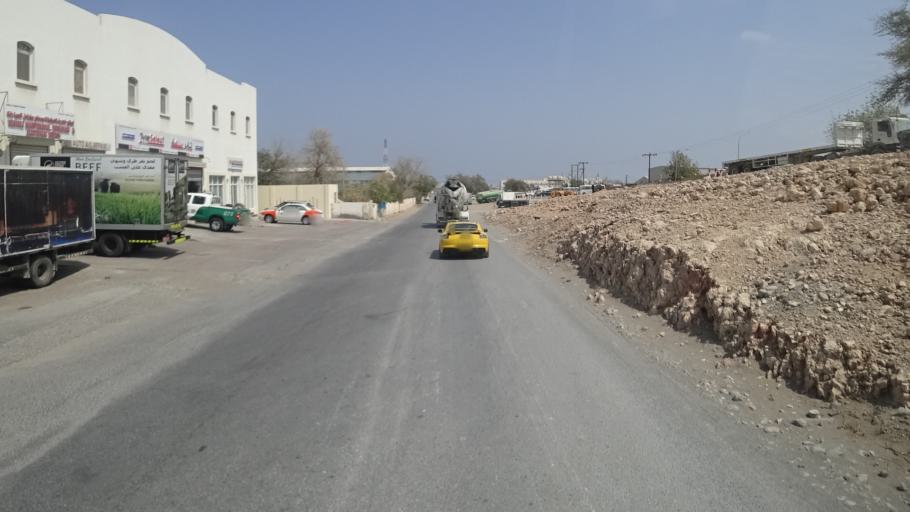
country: OM
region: Muhafazat Masqat
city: Bawshar
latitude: 23.5738
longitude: 58.3468
